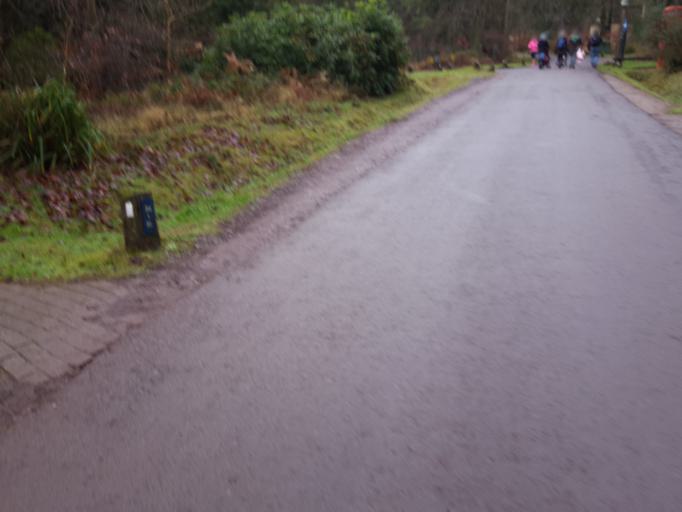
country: GB
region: England
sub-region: Wiltshire
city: Corsley
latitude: 51.1880
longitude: -2.2367
